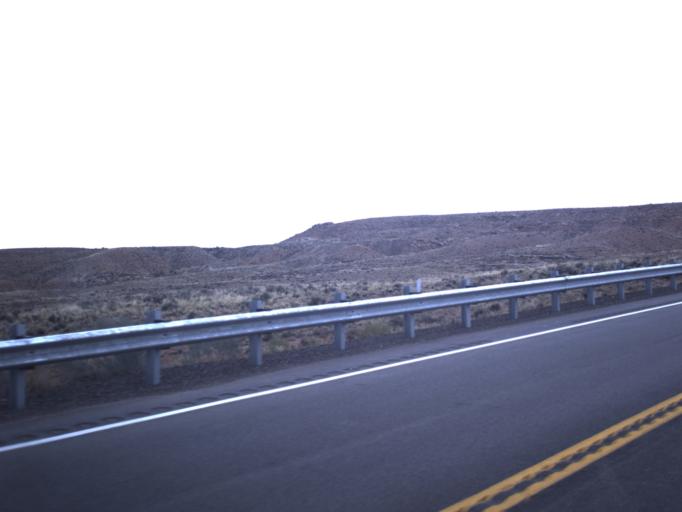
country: US
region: Utah
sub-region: Uintah County
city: Naples
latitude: 40.2998
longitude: -109.4769
